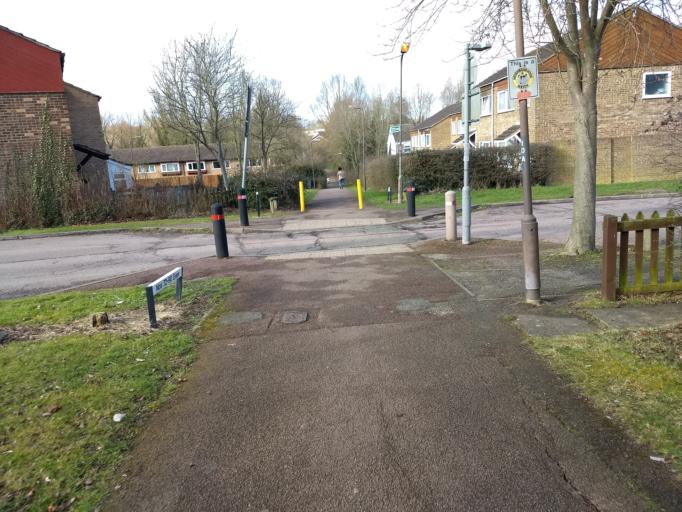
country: GB
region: England
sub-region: Milton Keynes
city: Milton Keynes
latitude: 52.0296
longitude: -0.7388
